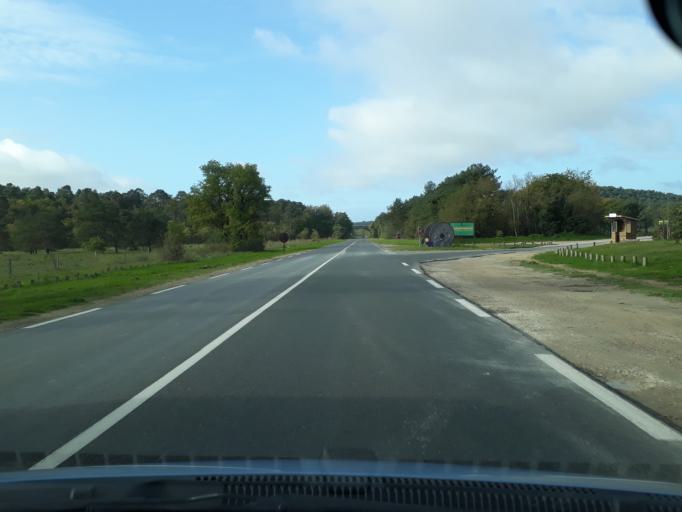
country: FR
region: Ile-de-France
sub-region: Departement de Seine-et-Marne
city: Fontainebleau
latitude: 48.3911
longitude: 2.6765
